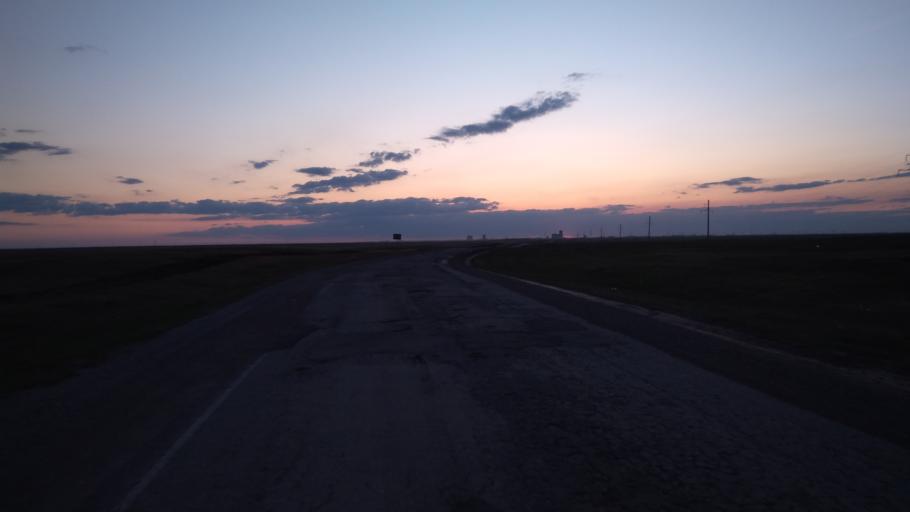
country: RU
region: Chelyabinsk
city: Troitsk
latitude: 54.0871
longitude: 61.6584
